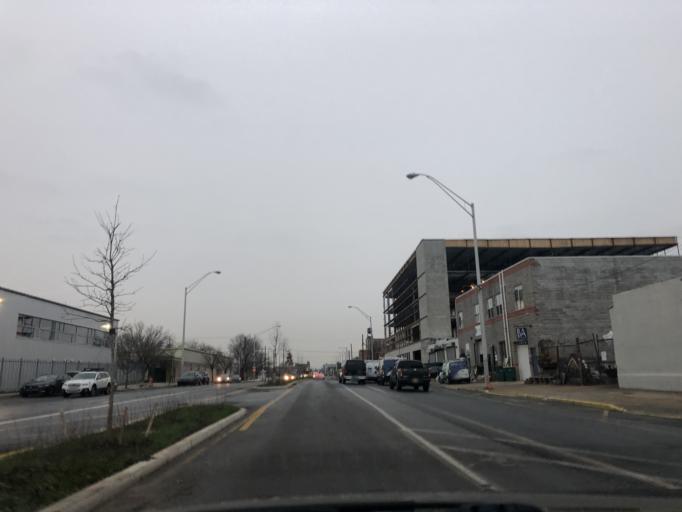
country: US
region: Pennsylvania
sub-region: Philadelphia County
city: Philadelphia
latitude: 39.9749
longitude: -75.1397
